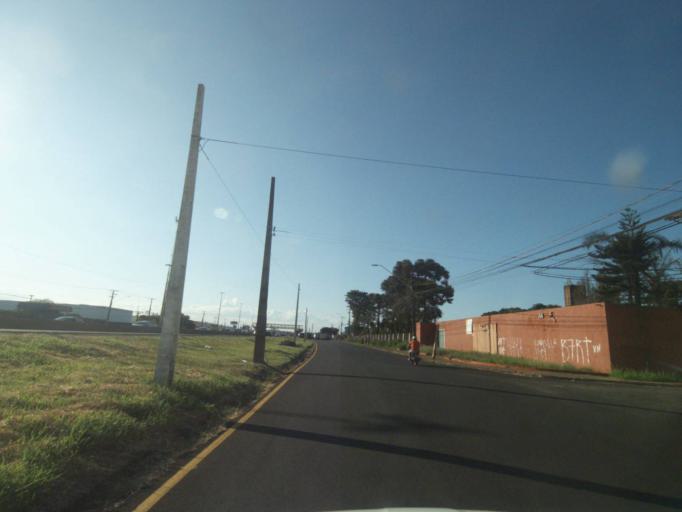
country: BR
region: Parana
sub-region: Cambe
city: Cambe
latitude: -23.3004
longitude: -51.2271
